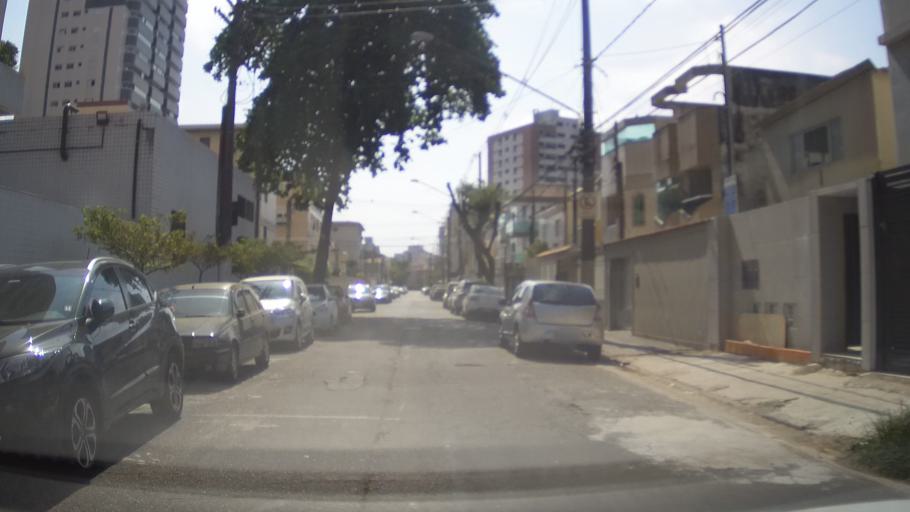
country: BR
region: Sao Paulo
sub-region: Guaruja
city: Guaruja
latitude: -23.9812
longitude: -46.2961
